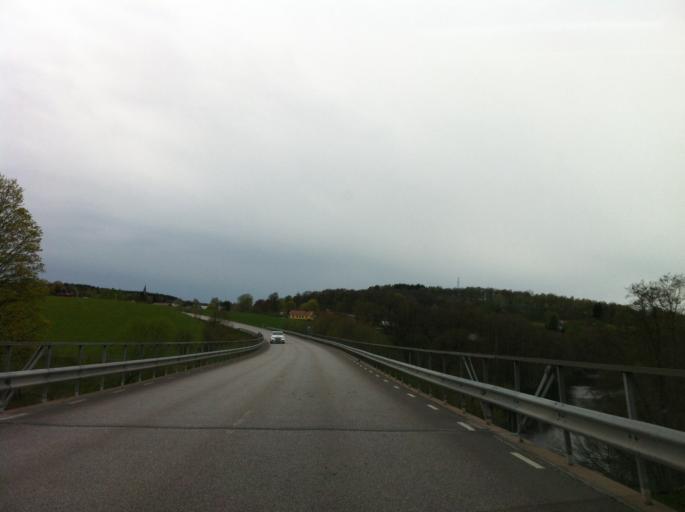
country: SE
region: Halland
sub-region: Falkenbergs Kommun
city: Falkenberg
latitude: 57.0693
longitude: 12.6568
